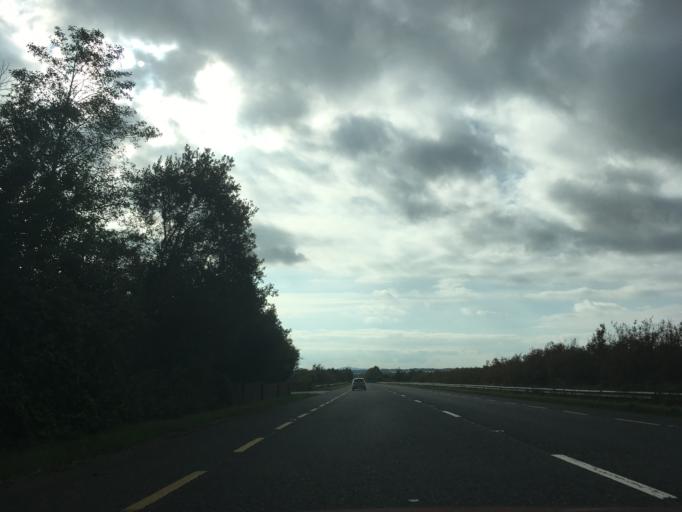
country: IE
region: Leinster
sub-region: Loch Garman
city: Loch Garman
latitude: 52.3448
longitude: -6.5925
